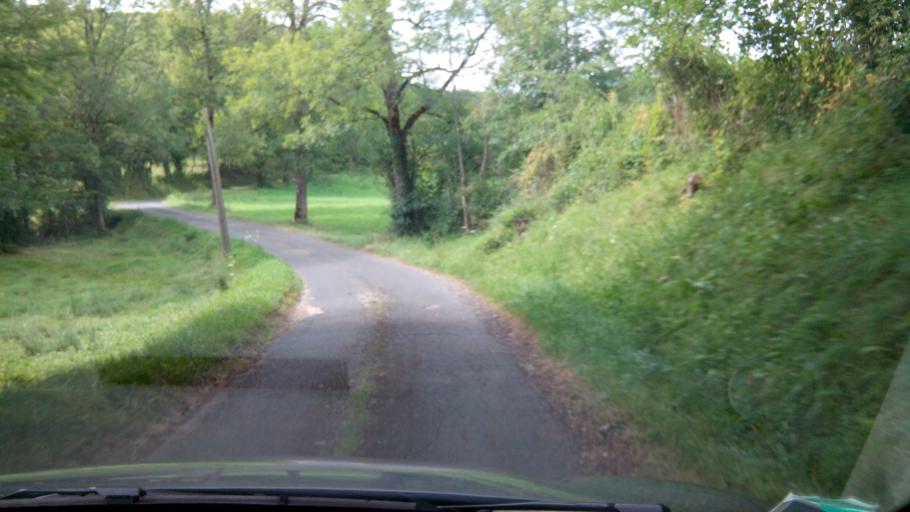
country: FR
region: Limousin
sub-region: Departement de la Correze
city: Cosnac
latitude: 45.0619
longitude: 1.5778
